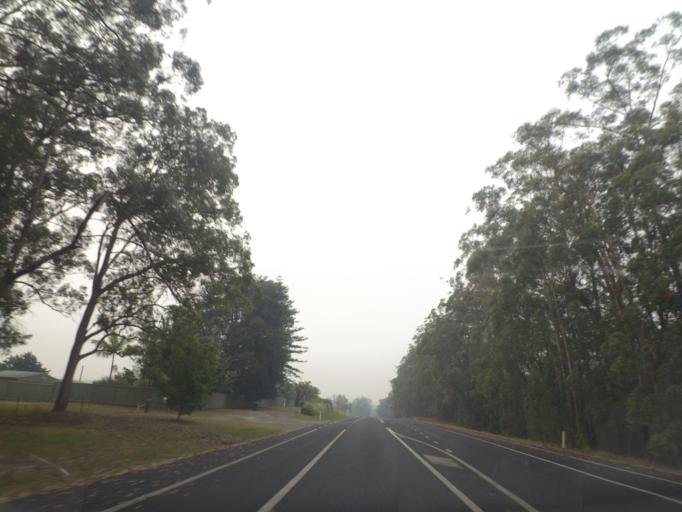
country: AU
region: New South Wales
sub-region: Coffs Harbour
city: Bonville
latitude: -30.4028
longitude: 153.0301
